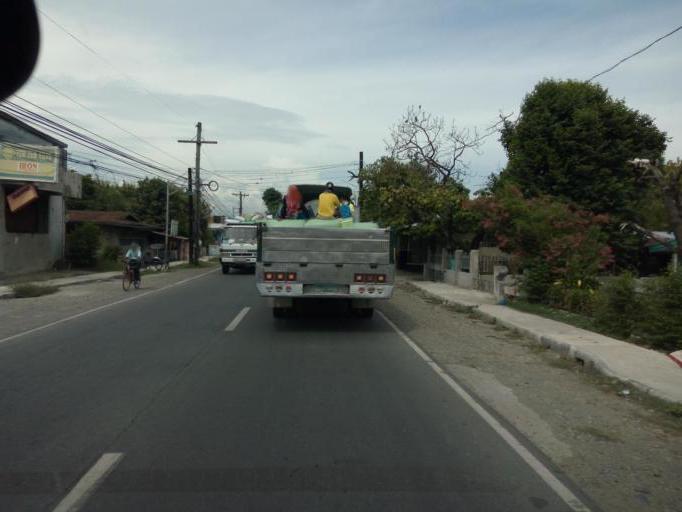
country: PH
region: Ilocos
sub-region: Province of Pangasinan
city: Rosales
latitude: 15.8934
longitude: 120.6362
